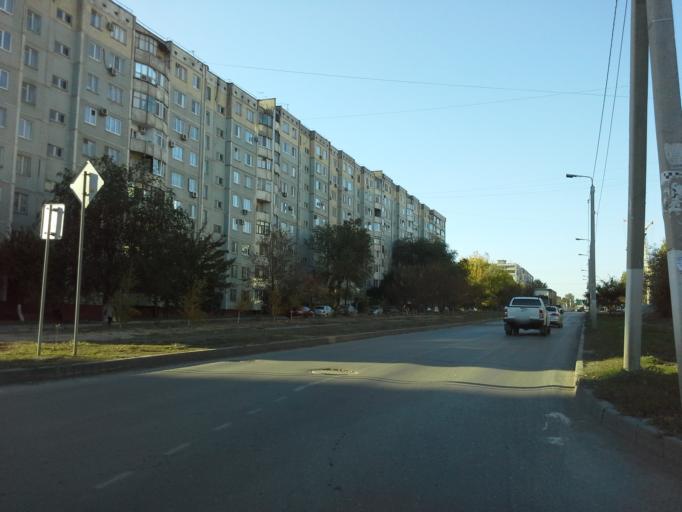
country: RU
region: Volgograd
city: Vodstroy
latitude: 48.8154
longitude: 44.6207
